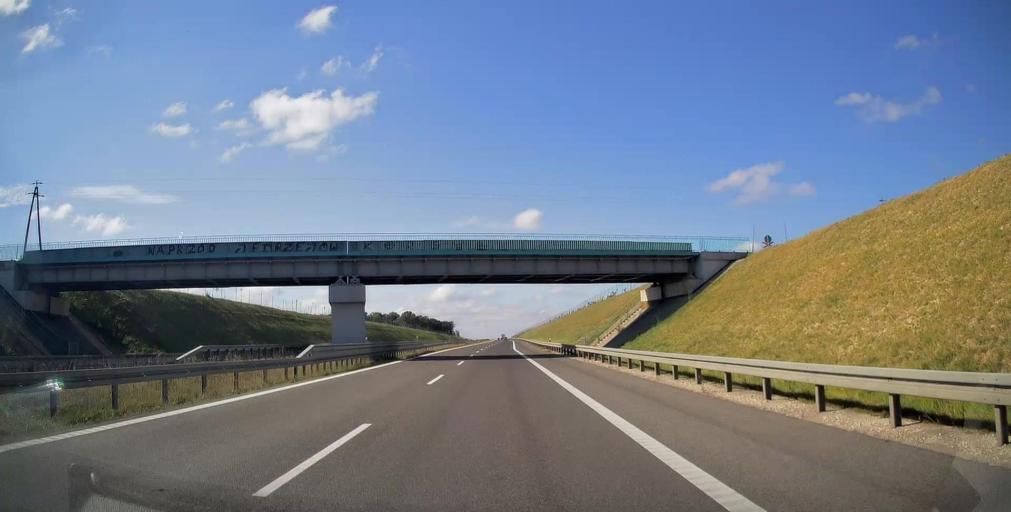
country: PL
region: Swietokrzyskie
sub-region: Powiat jedrzejowski
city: Jedrzejow
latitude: 50.6159
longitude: 20.2756
